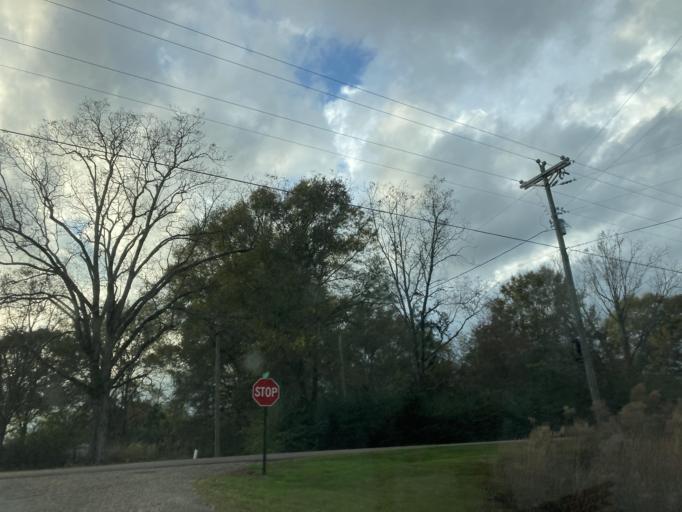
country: US
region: Mississippi
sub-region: Marion County
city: Columbia
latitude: 31.1961
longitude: -89.6342
